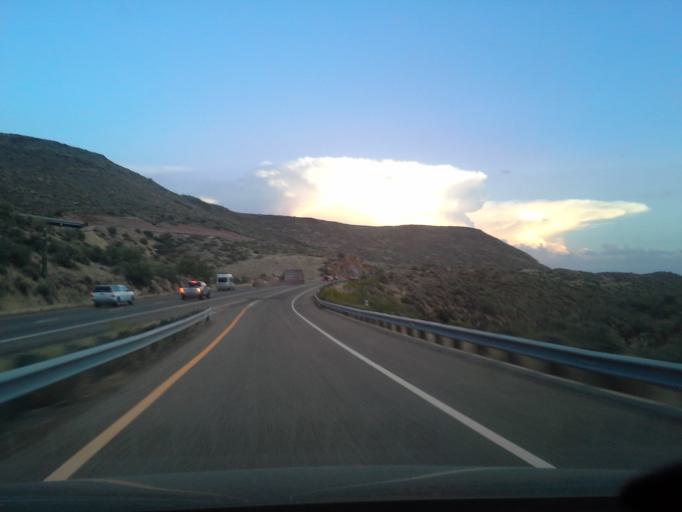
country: US
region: Arizona
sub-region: Yavapai County
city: Black Canyon City
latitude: 34.1393
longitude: -112.1489
